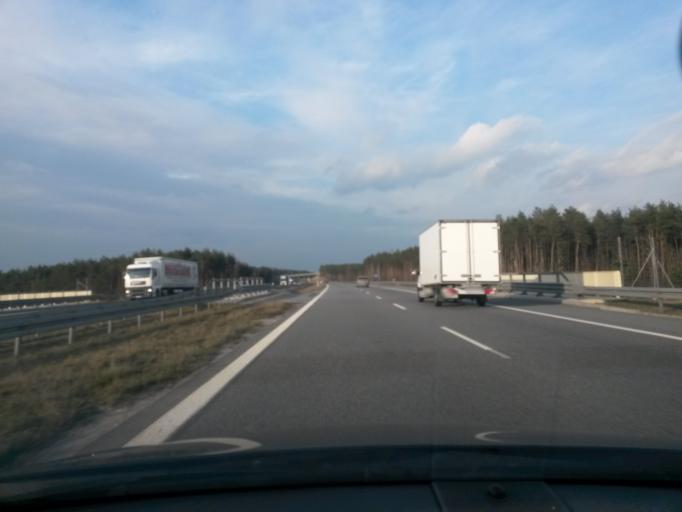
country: PL
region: Lodz Voivodeship
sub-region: powiat Lowicki
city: Domaniewice
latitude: 51.9502
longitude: 19.8392
